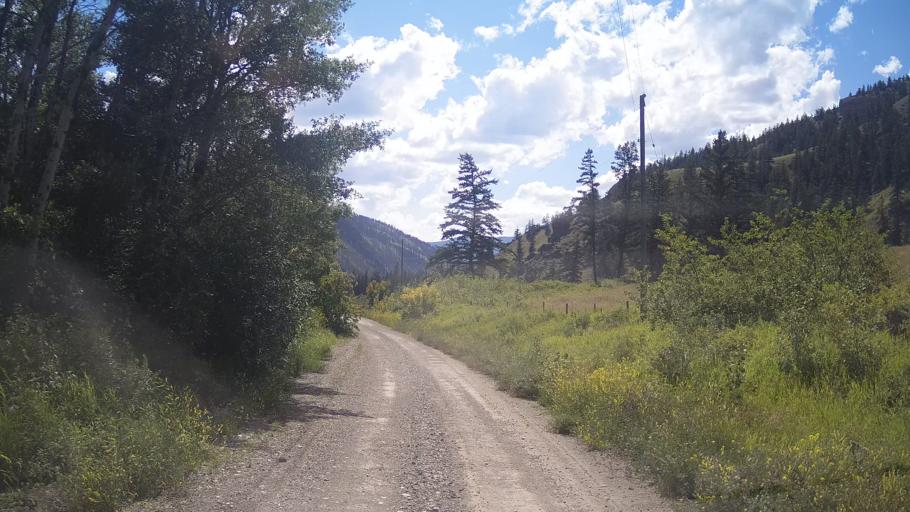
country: CA
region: British Columbia
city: Lillooet
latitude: 51.2381
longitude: -122.0470
